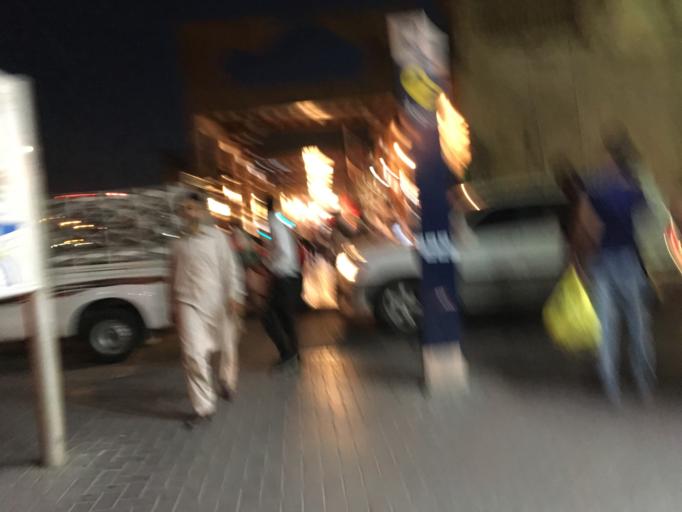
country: AE
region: Ash Shariqah
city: Sharjah
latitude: 25.2677
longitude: 55.2979
